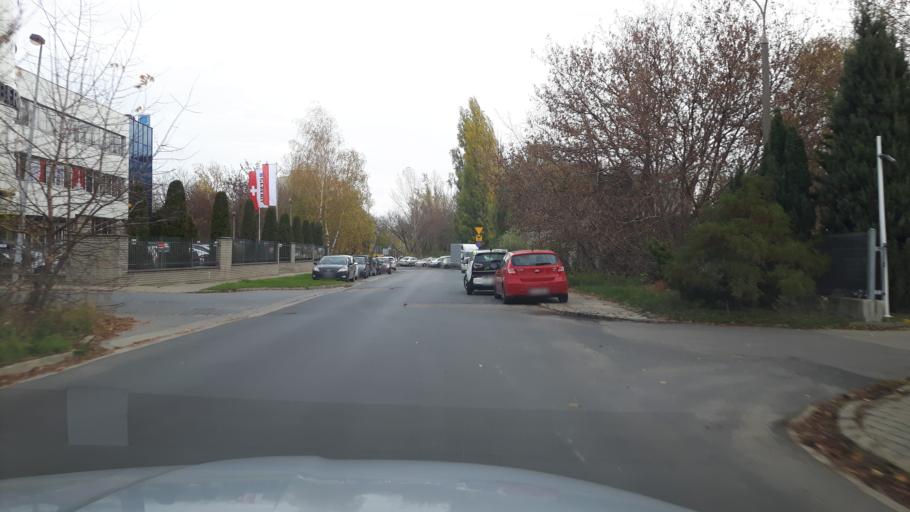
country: PL
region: Masovian Voivodeship
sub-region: Warszawa
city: Wlochy
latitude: 52.1710
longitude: 20.9906
